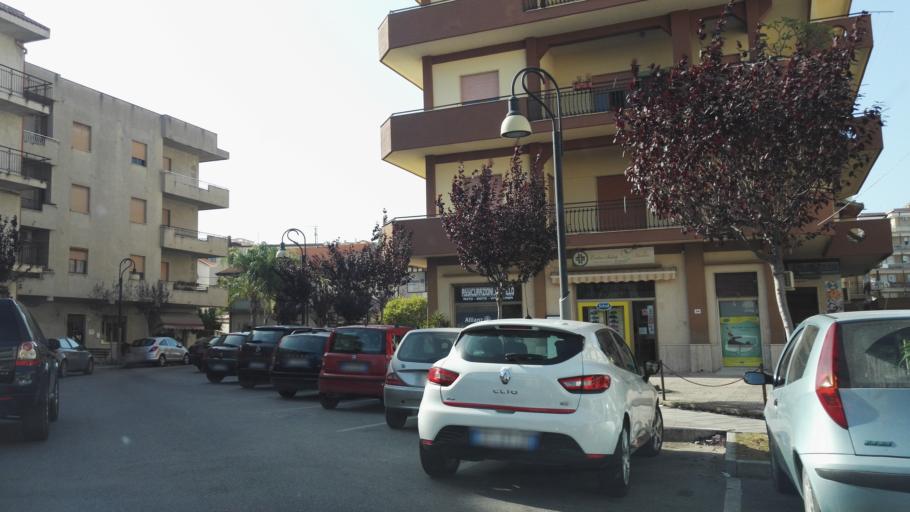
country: IT
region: Calabria
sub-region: Provincia di Reggio Calabria
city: Caulonia Marina
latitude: 38.3442
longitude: 16.4662
